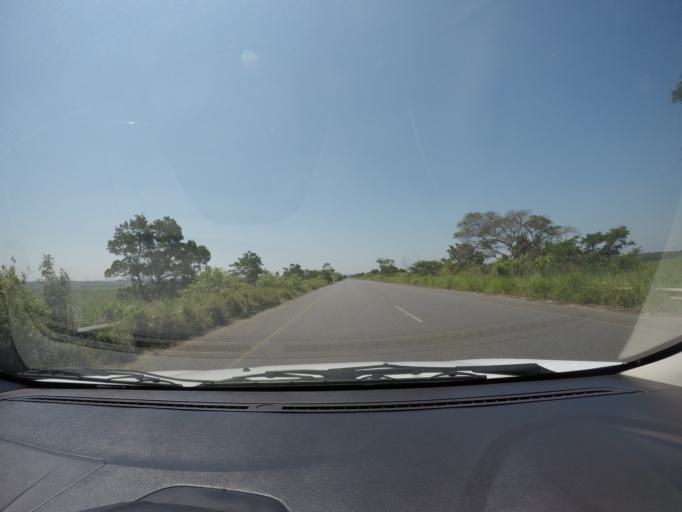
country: ZA
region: KwaZulu-Natal
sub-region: uThungulu District Municipality
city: Empangeni
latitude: -28.7855
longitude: 31.9580
